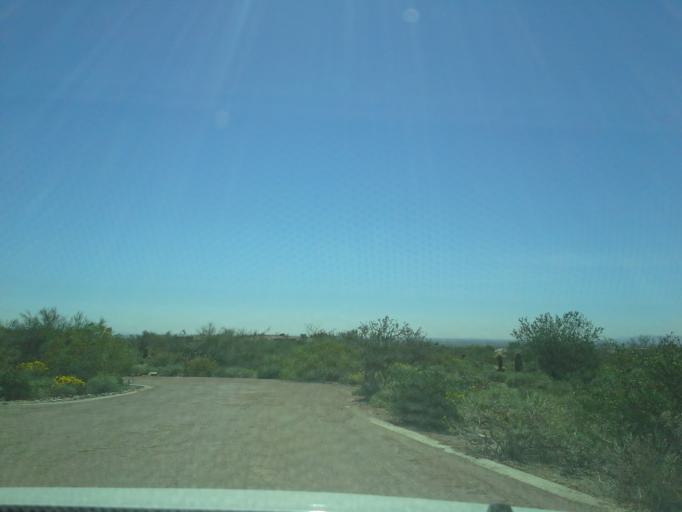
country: US
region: Arizona
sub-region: Maricopa County
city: Fountain Hills
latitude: 33.5993
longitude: -111.8139
